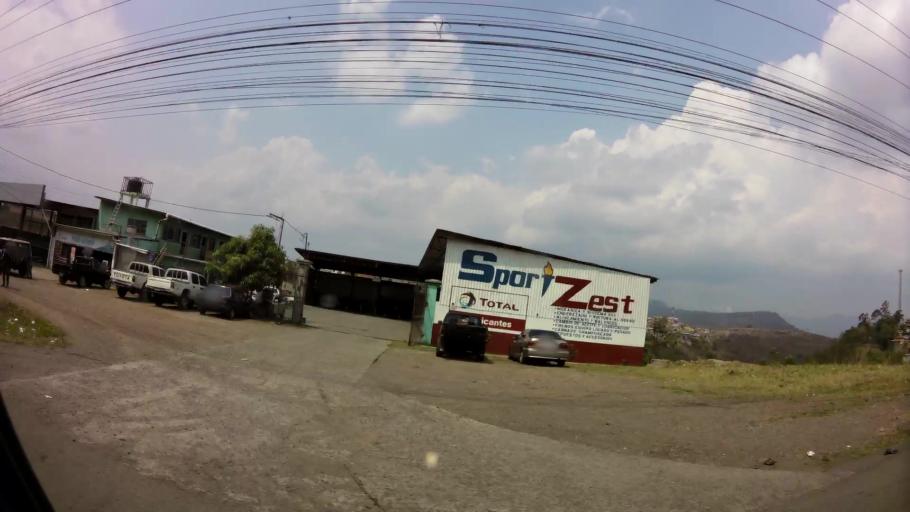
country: HN
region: Francisco Morazan
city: El Lolo
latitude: 14.1201
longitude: -87.2248
